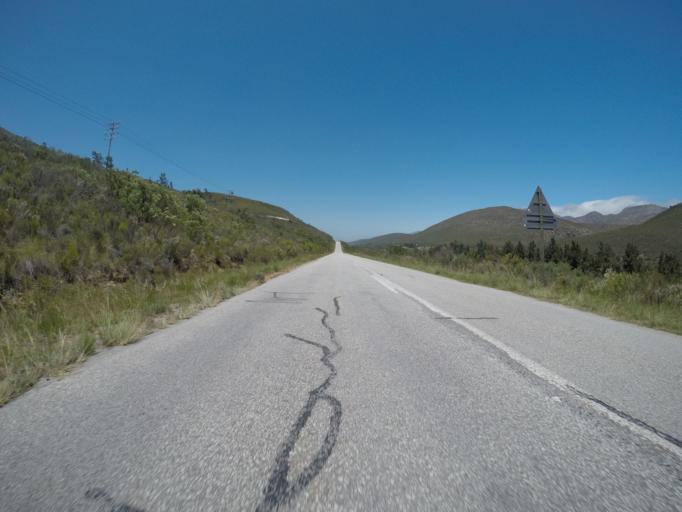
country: ZA
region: Eastern Cape
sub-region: Cacadu District Municipality
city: Kareedouw
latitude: -33.8646
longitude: 24.0085
